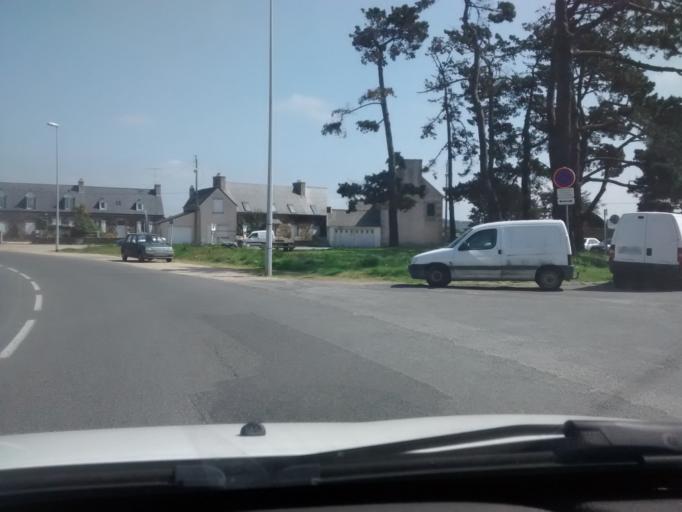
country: FR
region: Brittany
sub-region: Departement des Cotes-d'Armor
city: Perros-Guirec
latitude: 48.8061
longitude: -3.4384
